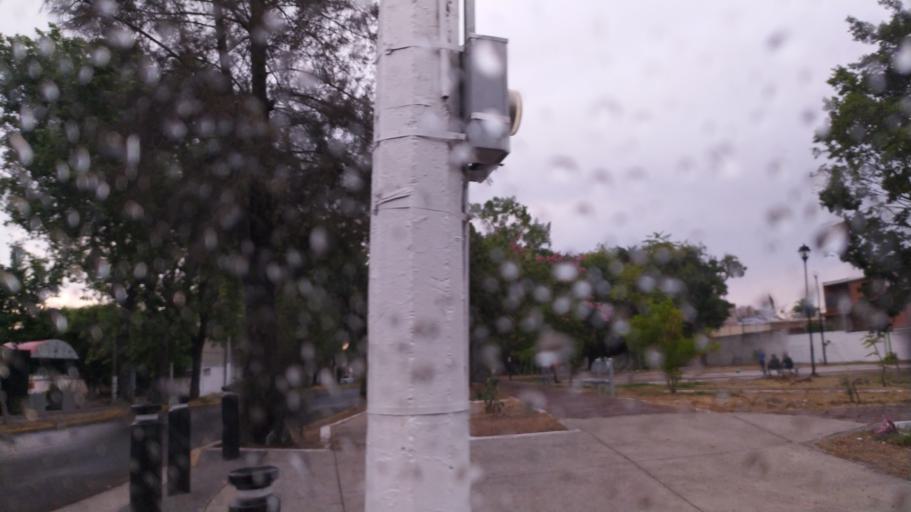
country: MX
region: Jalisco
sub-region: Zapopan
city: Zapopan
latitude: 20.7209
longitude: -103.3632
